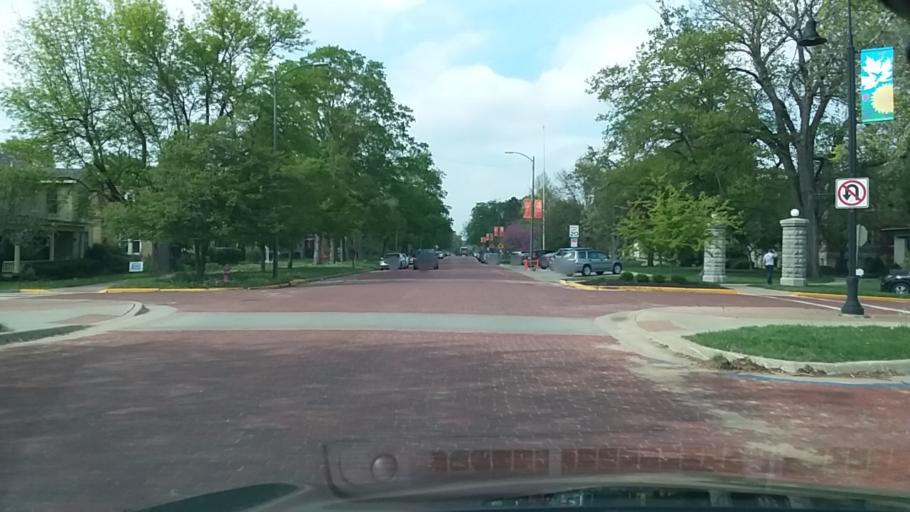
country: US
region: Kansas
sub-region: Douglas County
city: Baldwin City
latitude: 38.7757
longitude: -95.1889
